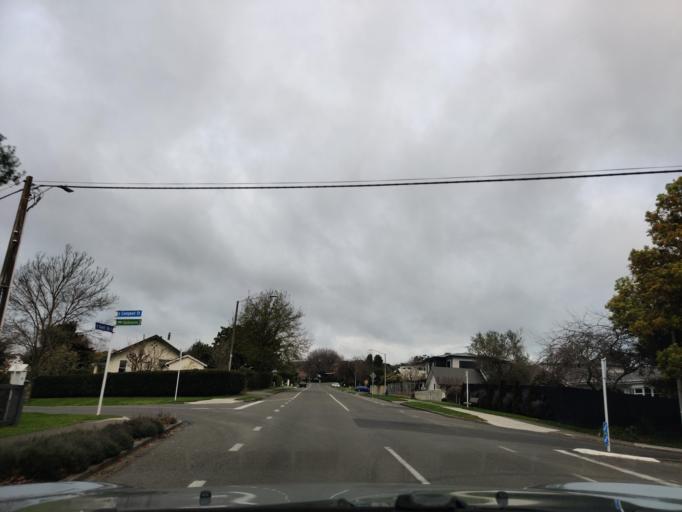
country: NZ
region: Hawke's Bay
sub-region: Hastings District
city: Hastings
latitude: -39.6702
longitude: 176.8830
